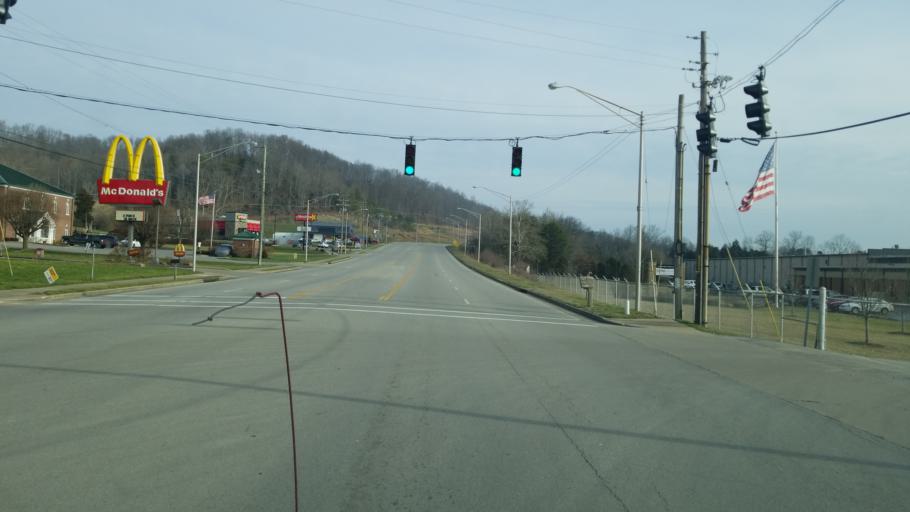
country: US
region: Kentucky
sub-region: Casey County
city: Liberty
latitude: 37.3233
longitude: -84.9249
